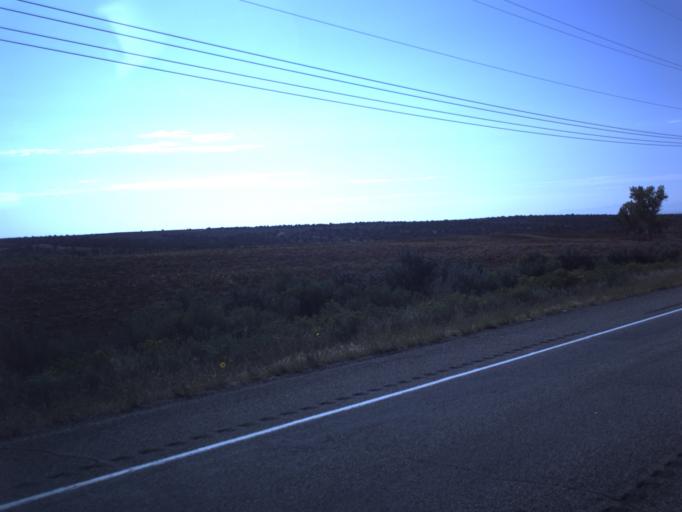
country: US
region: Utah
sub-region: San Juan County
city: Blanding
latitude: 37.5574
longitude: -109.4895
